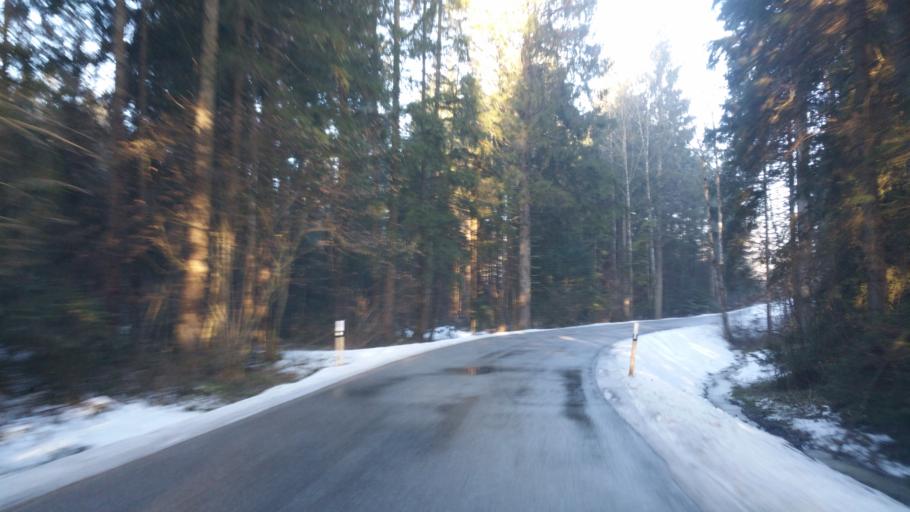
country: DE
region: Bavaria
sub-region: Upper Bavaria
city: Bichl
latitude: 47.7551
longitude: 11.4203
